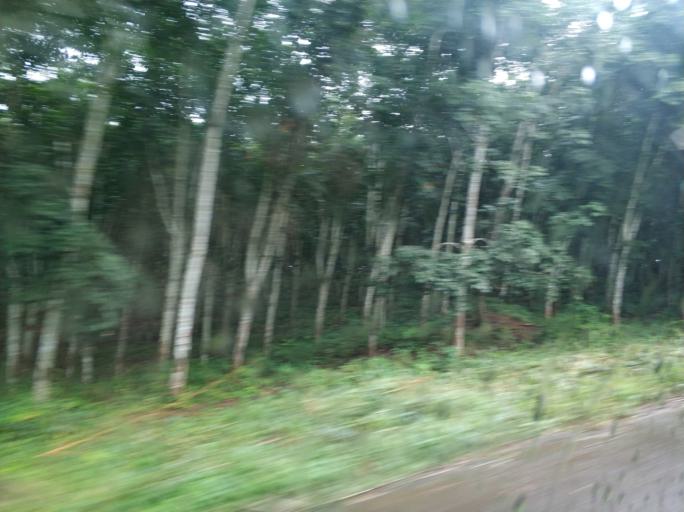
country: NG
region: Ogun
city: Abigi
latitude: 6.7080
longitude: 4.4597
